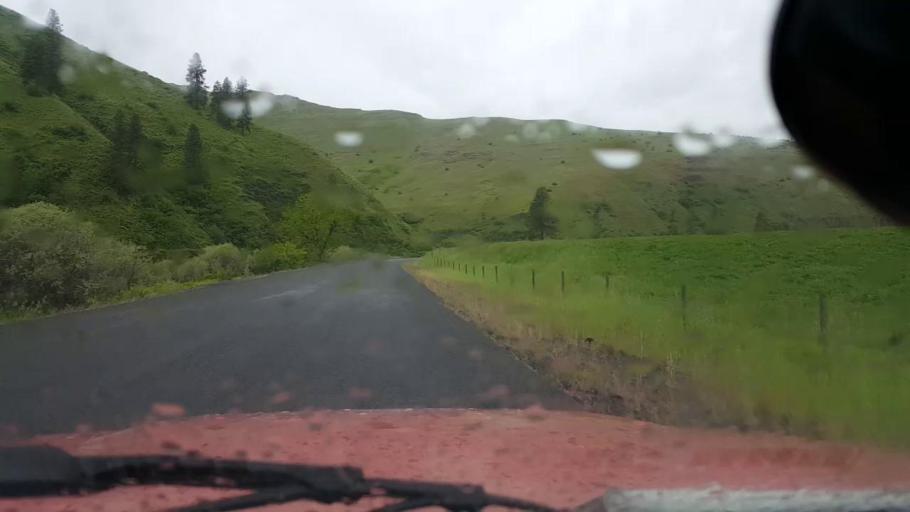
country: US
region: Washington
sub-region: Asotin County
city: Asotin
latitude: 46.0283
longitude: -117.3088
